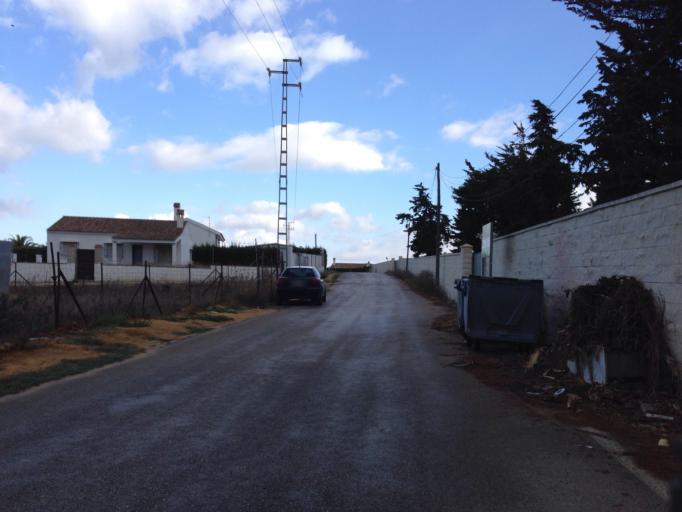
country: ES
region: Andalusia
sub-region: Provincia de Cadiz
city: Conil de la Frontera
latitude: 36.3016
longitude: -6.1117
